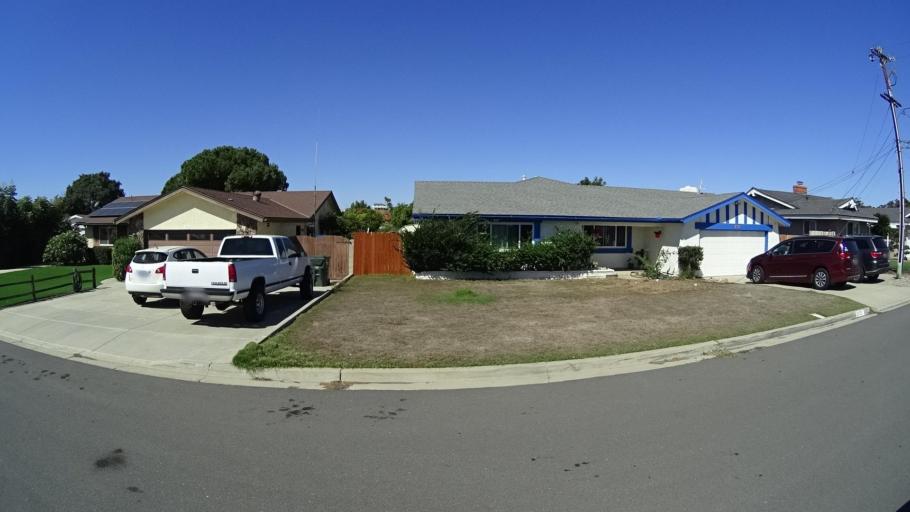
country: US
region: California
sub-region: San Diego County
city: Bonita
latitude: 32.6563
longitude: -117.0588
